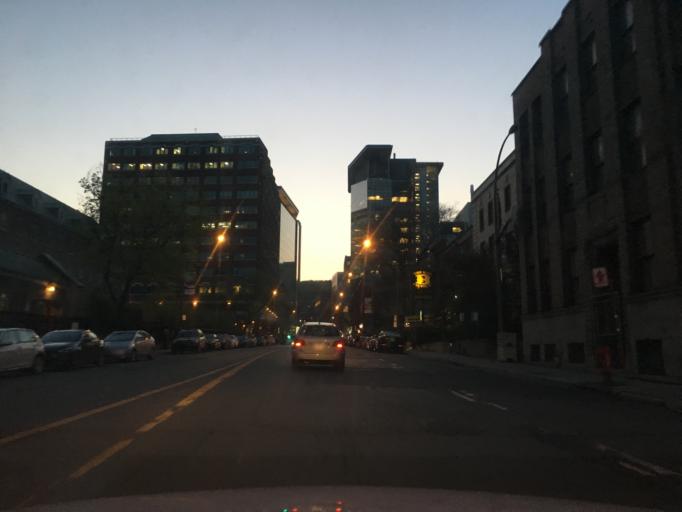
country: CA
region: Quebec
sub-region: Montreal
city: Montreal
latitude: 45.4941
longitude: -73.5756
